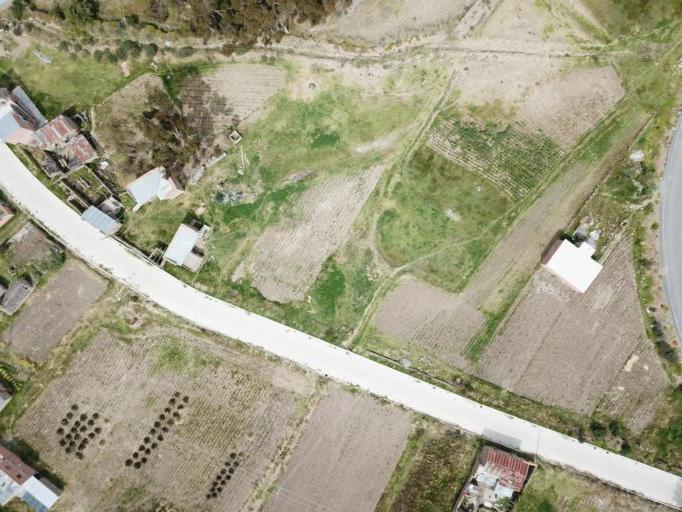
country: BO
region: La Paz
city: Achacachi
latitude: -16.0521
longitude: -68.8160
